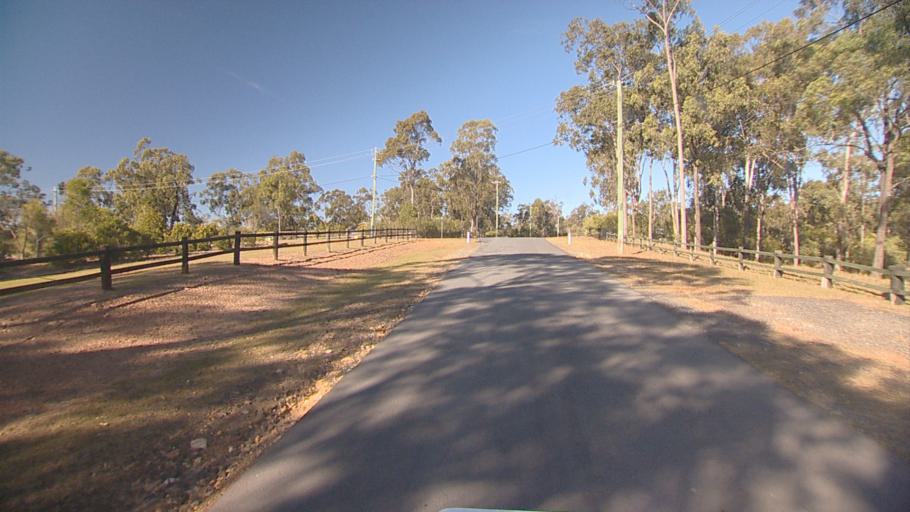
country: AU
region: Queensland
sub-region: Ipswich
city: Springfield Lakes
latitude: -27.6998
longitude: 152.9299
